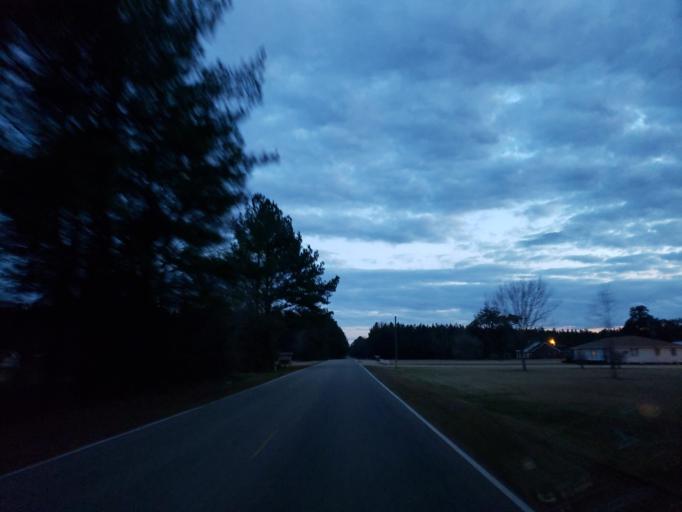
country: US
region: Mississippi
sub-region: Forrest County
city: Hattiesburg
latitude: 31.2677
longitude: -89.2411
